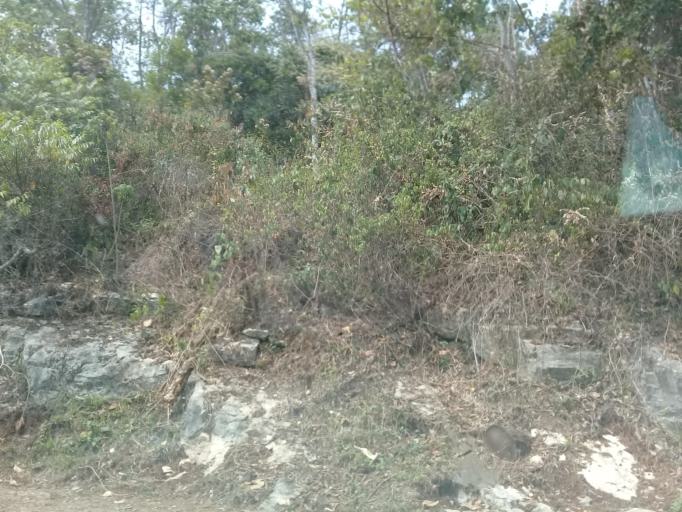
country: MX
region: Veracruz
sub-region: Tezonapa
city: Laguna Chica (Pueblo Nuevo)
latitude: 18.5813
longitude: -96.7513
